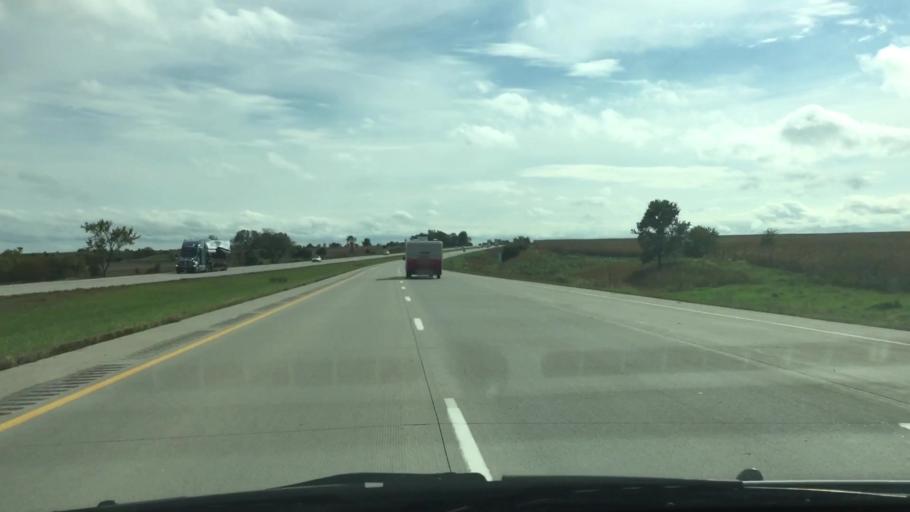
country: US
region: Iowa
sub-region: Clarke County
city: Osceola
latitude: 40.9676
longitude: -93.7975
